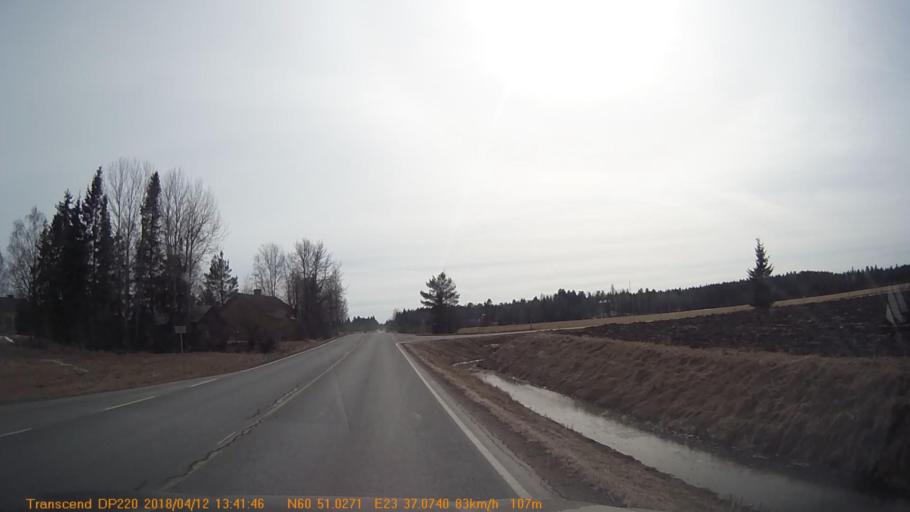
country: FI
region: Haeme
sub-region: Forssa
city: Forssa
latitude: 60.8496
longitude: 23.6179
